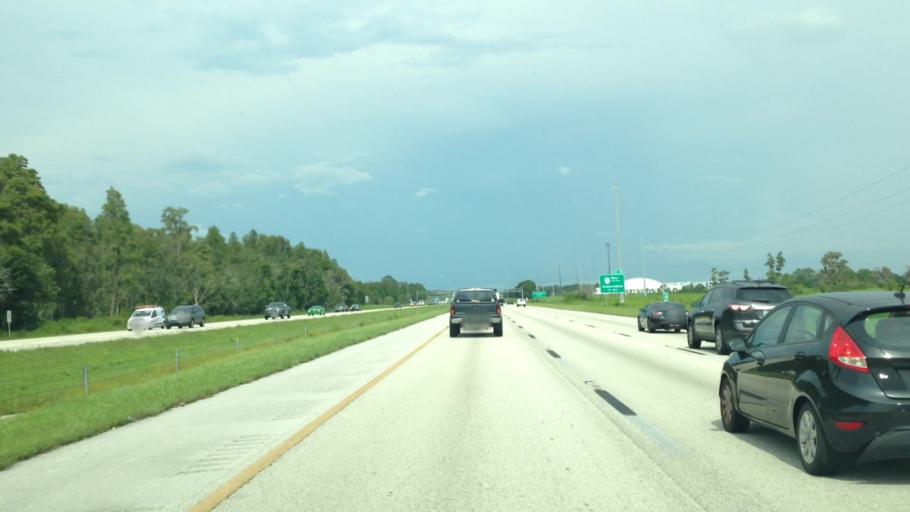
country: US
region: Florida
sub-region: Polk County
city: Polk City
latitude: 28.1483
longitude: -81.8671
